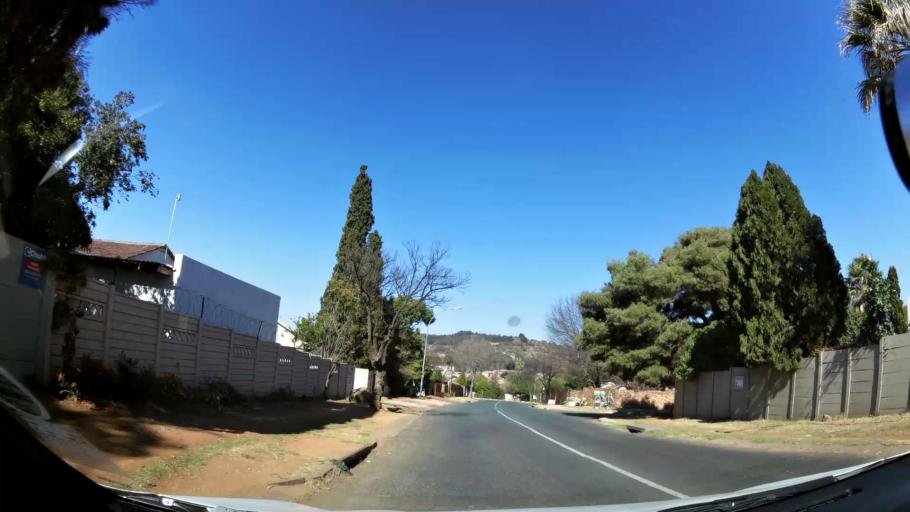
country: ZA
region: Gauteng
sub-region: City of Johannesburg Metropolitan Municipality
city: Johannesburg
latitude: -26.2734
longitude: 27.9872
